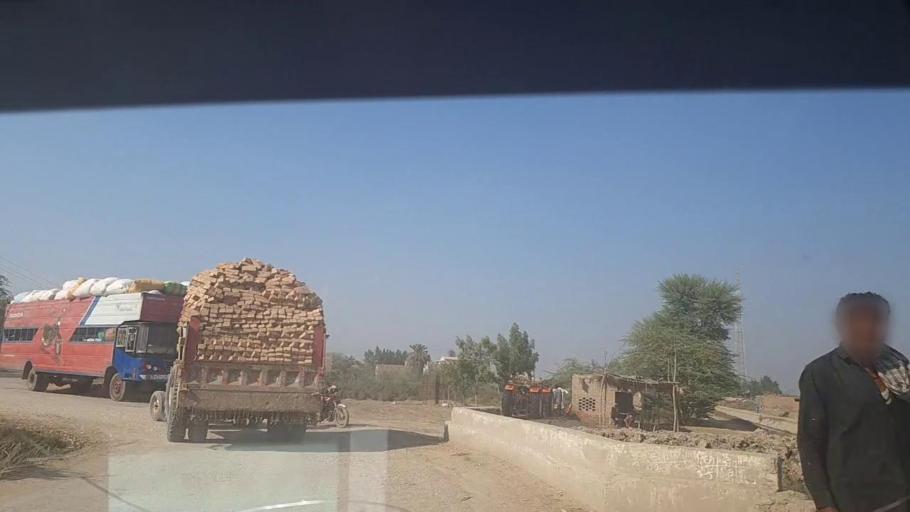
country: PK
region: Sindh
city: Kot Diji
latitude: 27.4387
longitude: 68.6342
